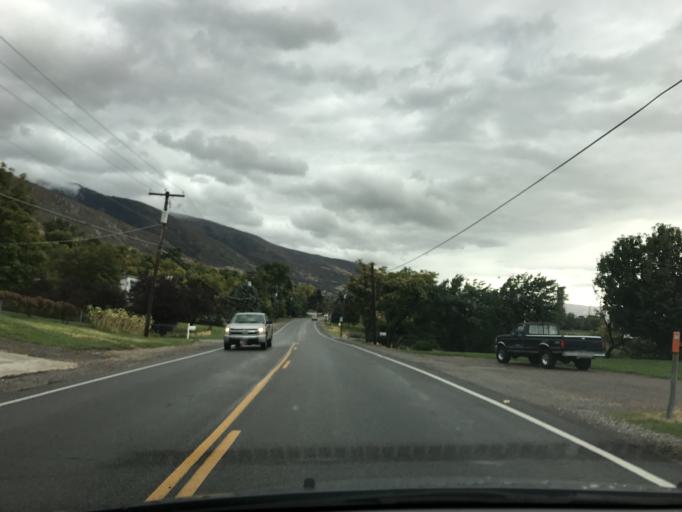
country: US
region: Utah
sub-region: Davis County
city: Farmington
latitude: 40.9962
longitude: -111.8971
